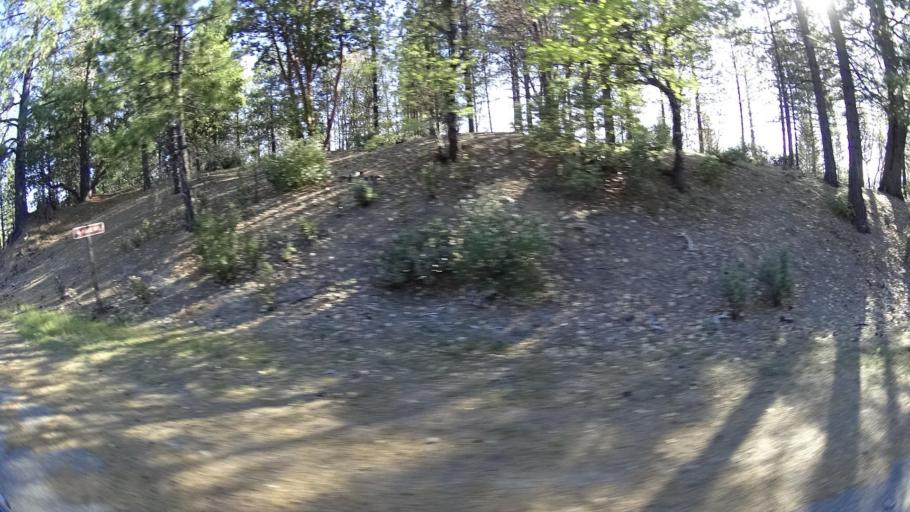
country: US
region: California
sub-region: Lake County
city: Upper Lake
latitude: 39.3122
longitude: -122.9433
